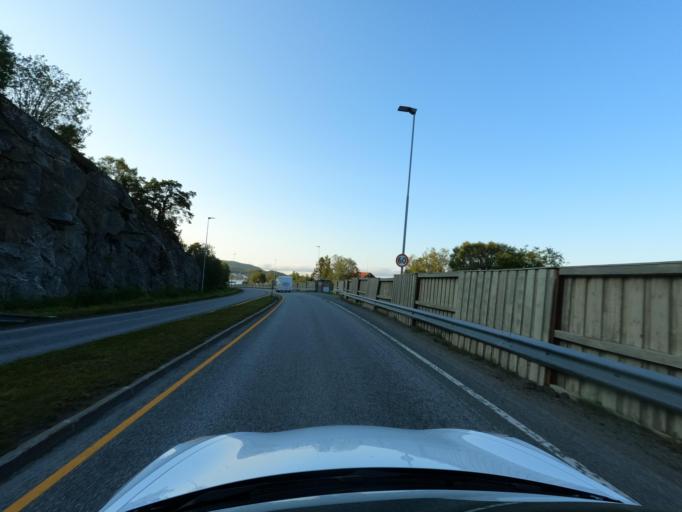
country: NO
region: Troms
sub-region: Harstad
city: Harstad
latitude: 68.7570
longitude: 16.5678
